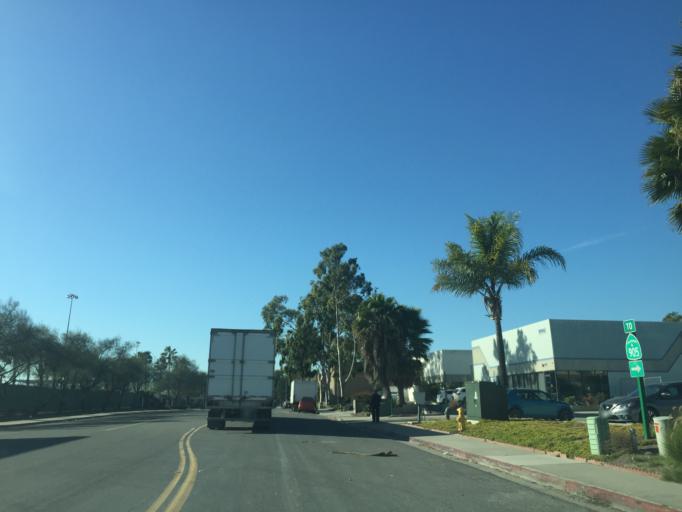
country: MX
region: Baja California
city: Tijuana
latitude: 32.5530
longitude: -116.9341
